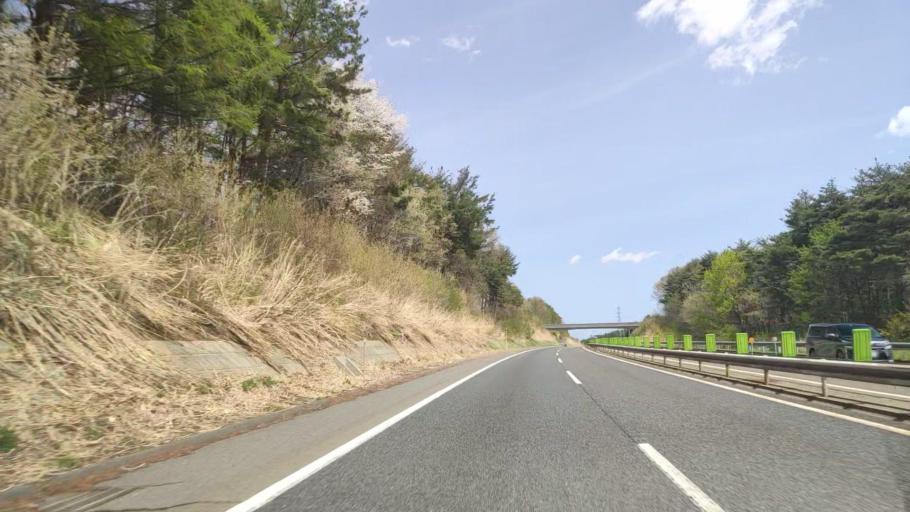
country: JP
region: Aomori
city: Hachinohe
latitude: 40.4299
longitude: 141.4412
